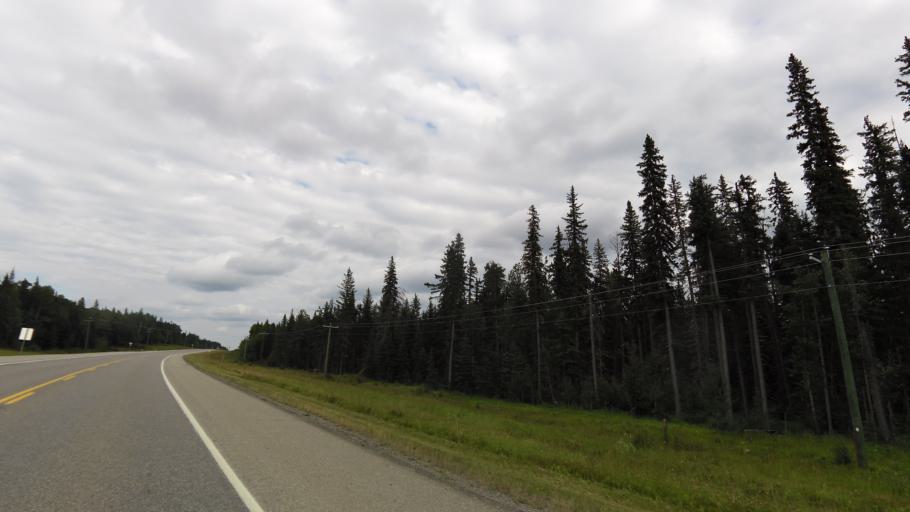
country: CA
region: Alberta
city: Rocky Mountain House
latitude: 52.5013
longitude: -115.4966
